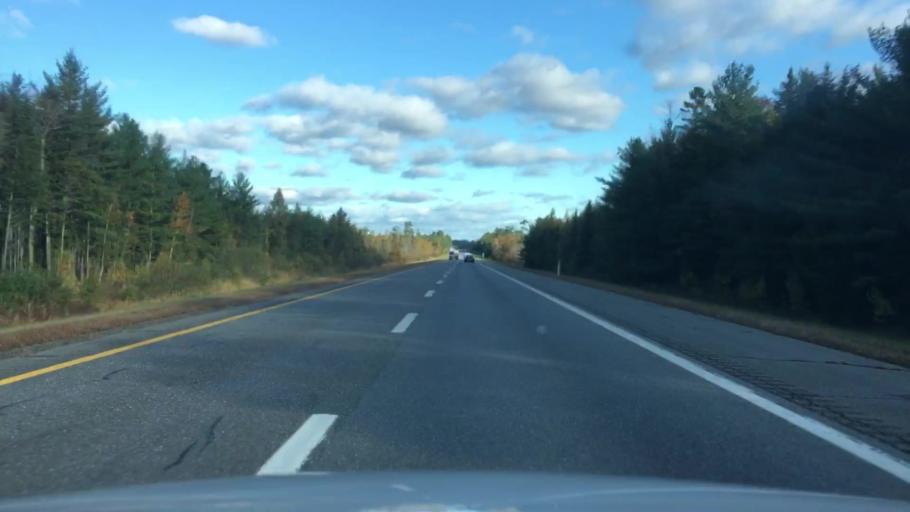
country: US
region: Maine
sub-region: Penobscot County
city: Greenbush
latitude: 45.1277
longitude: -68.6958
